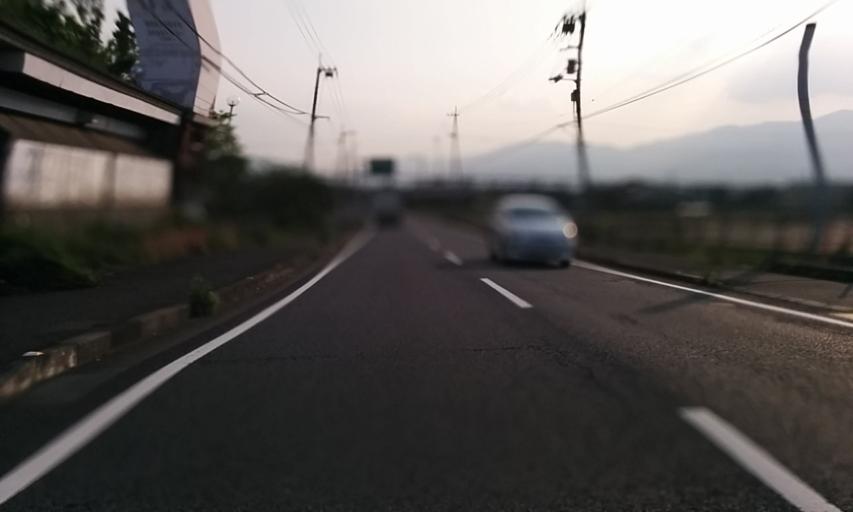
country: JP
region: Ehime
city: Saijo
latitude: 33.8943
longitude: 133.0945
